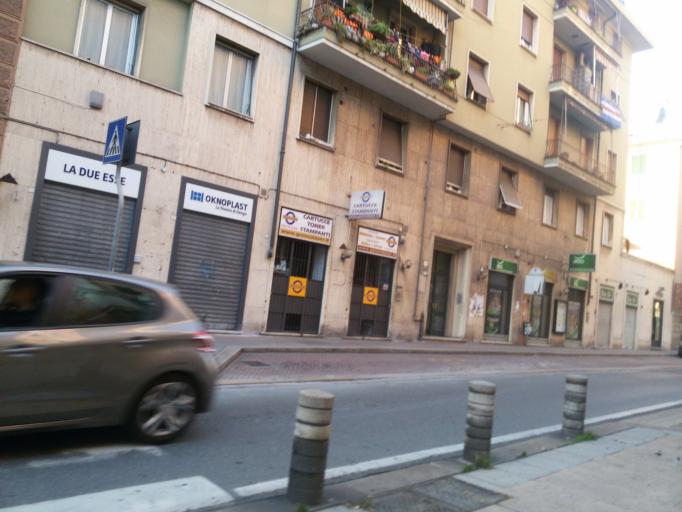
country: IT
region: Liguria
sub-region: Provincia di Genova
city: Genoa
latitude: 44.4312
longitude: 8.8920
